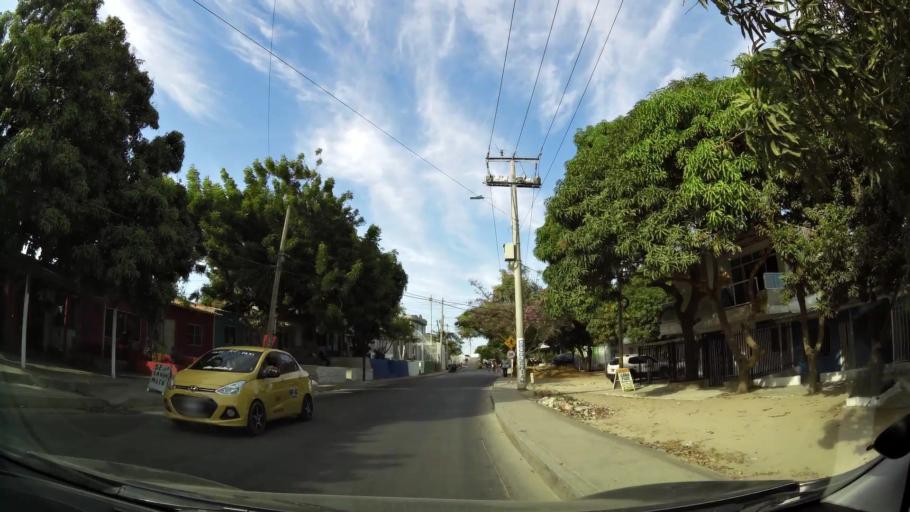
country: CO
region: Atlantico
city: Soledad
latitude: 10.9287
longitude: -74.8107
